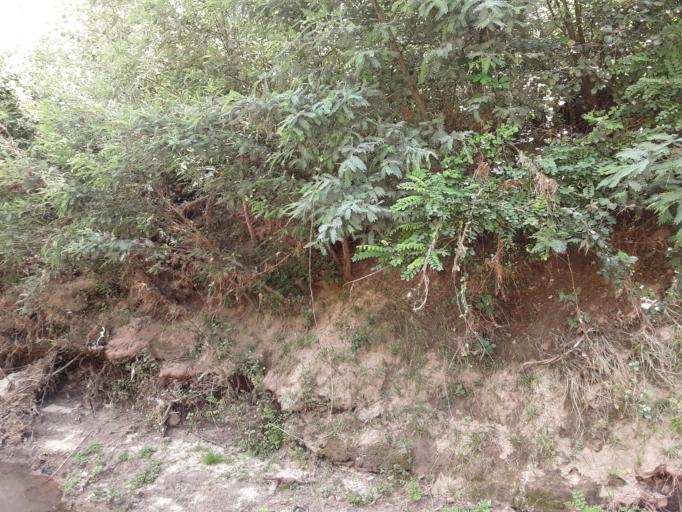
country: LS
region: Leribe
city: Leribe
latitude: -28.9573
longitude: 28.0095
